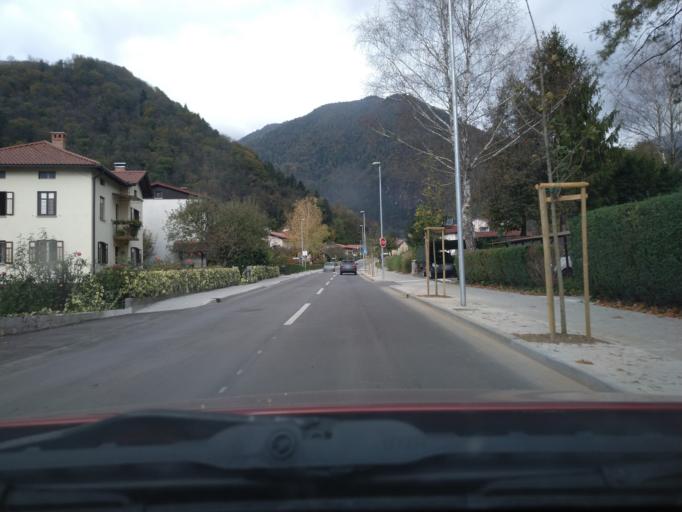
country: SI
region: Tolmin
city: Tolmin
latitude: 46.1863
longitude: 13.7318
